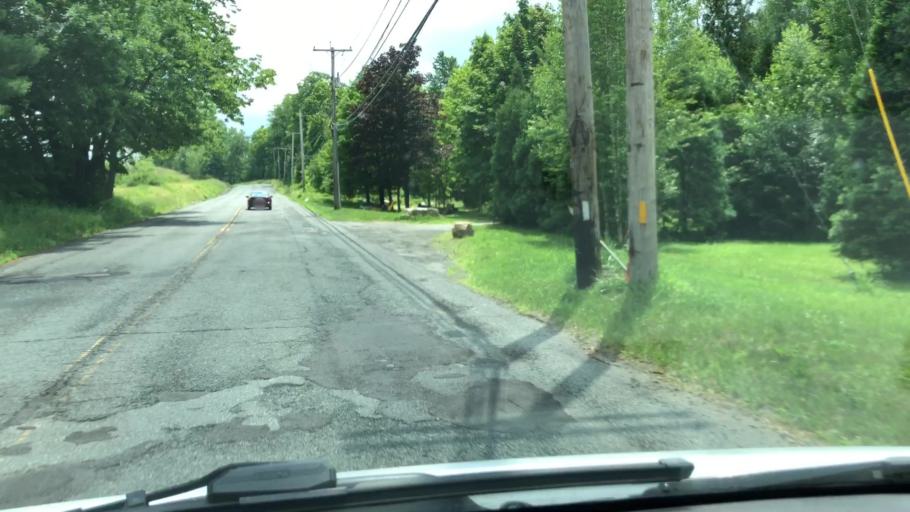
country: US
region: Massachusetts
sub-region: Berkshire County
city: Adams
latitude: 42.5960
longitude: -73.1180
